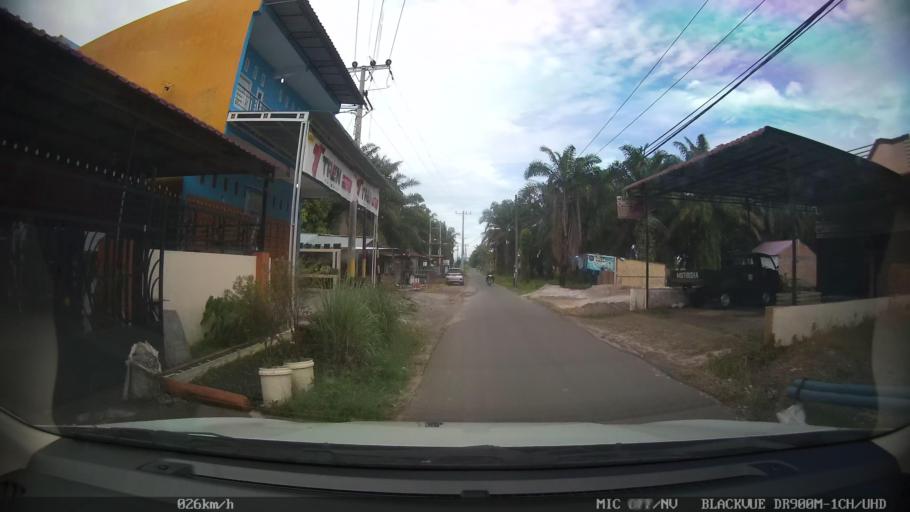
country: ID
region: North Sumatra
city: Sunggal
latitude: 3.5726
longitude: 98.5676
